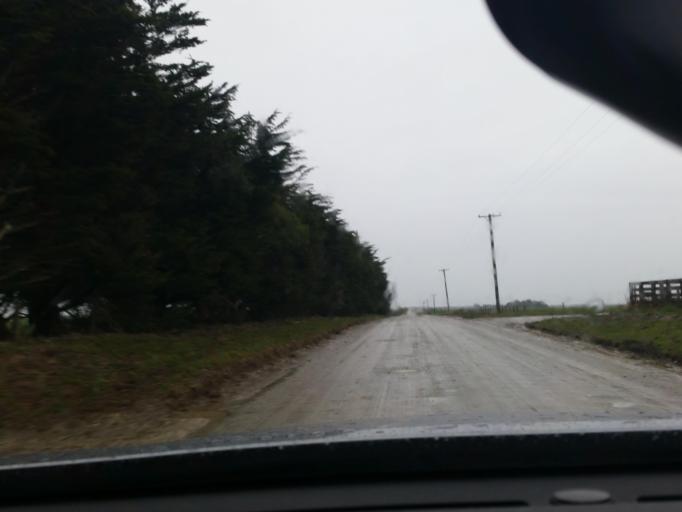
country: NZ
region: Southland
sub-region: Invercargill City
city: Invercargill
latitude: -46.4303
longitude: 168.5062
